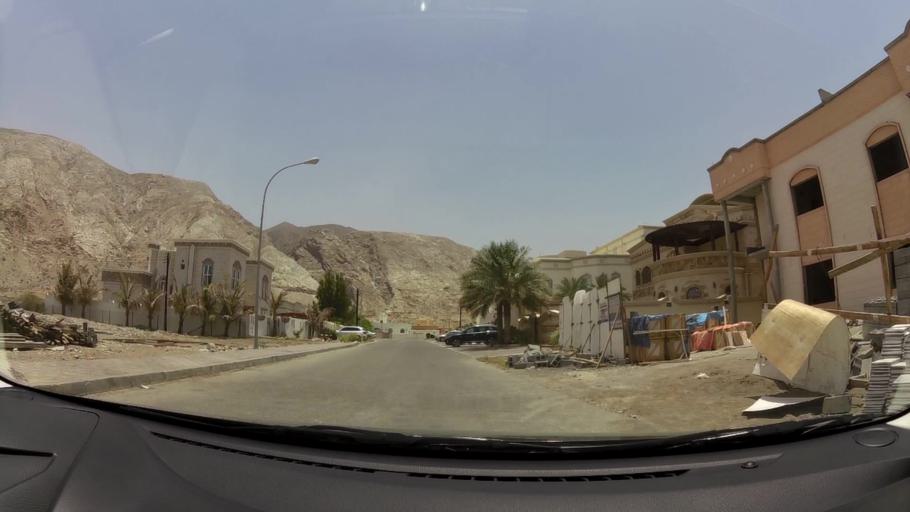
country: OM
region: Muhafazat Masqat
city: Bawshar
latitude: 23.5522
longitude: 58.4106
